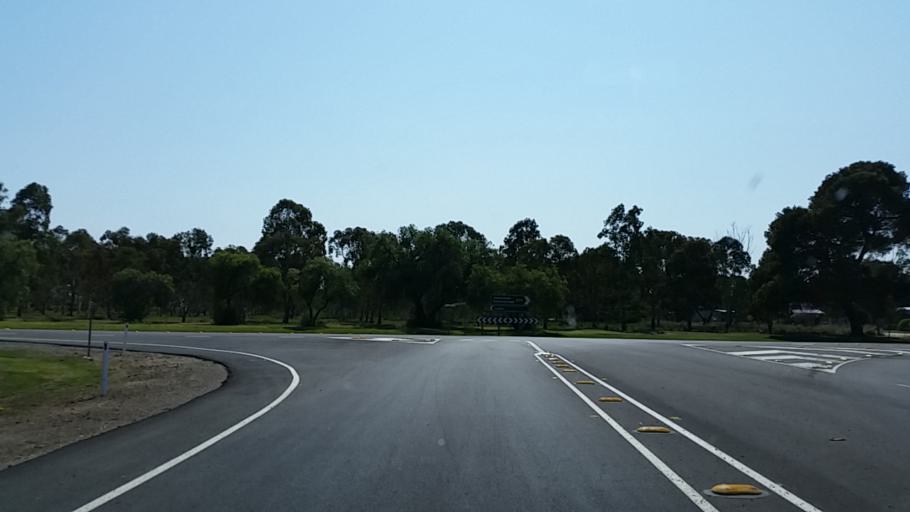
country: AU
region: South Australia
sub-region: Northern Areas
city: Jamestown
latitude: -33.1811
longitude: 138.4792
